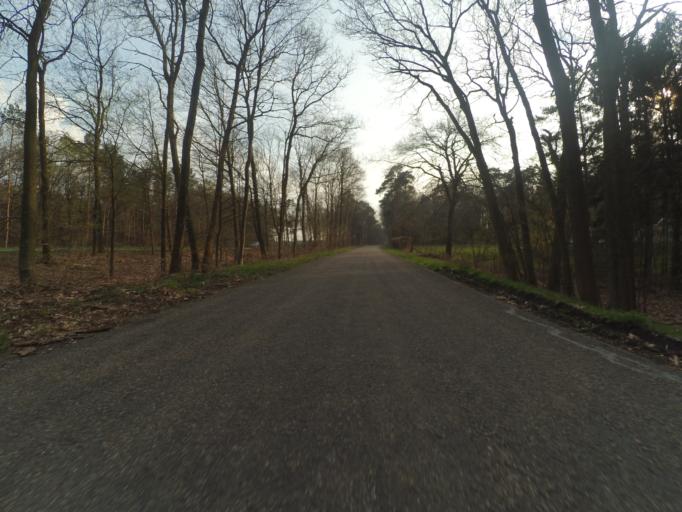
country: NL
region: Gelderland
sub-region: Gemeente Apeldoorn
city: Beekbergen
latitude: 52.1694
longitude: 5.9064
